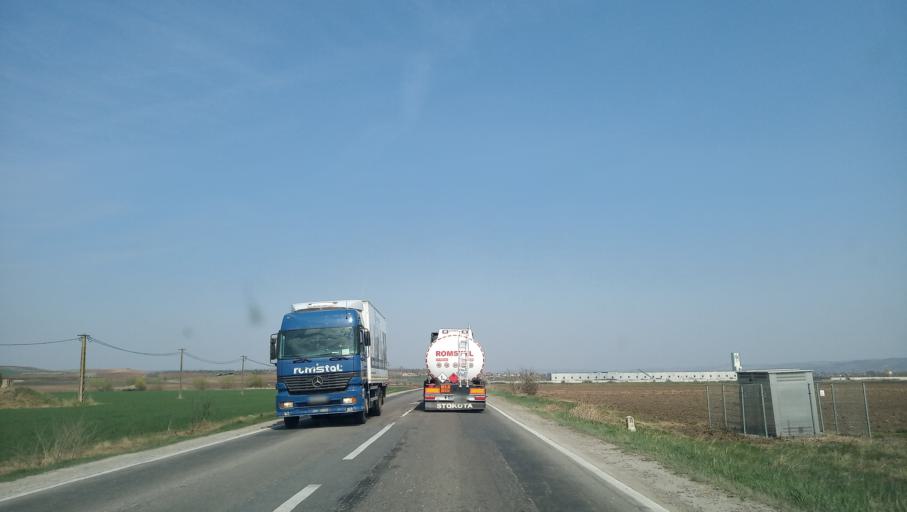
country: RO
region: Alba
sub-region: Oras Teius
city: Teius
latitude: 46.1821
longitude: 23.6579
